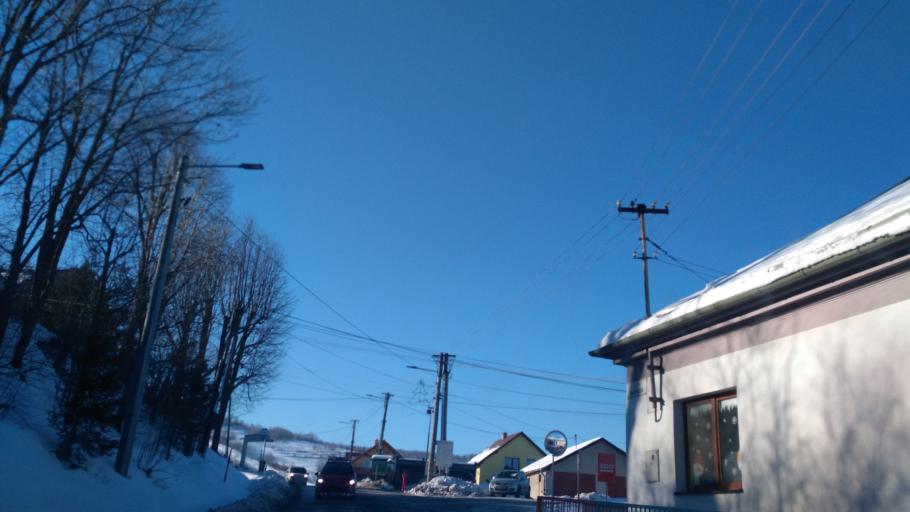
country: SK
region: Kosicky
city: Kosice
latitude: 48.7737
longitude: 21.2081
